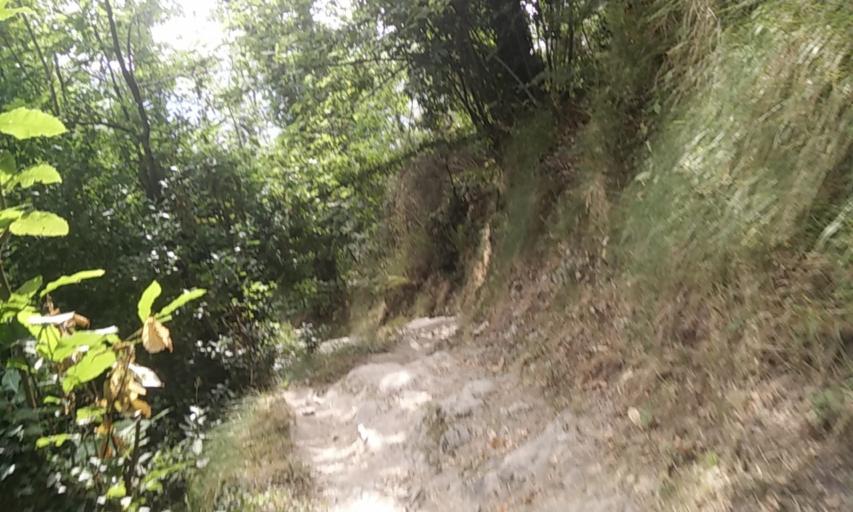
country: IT
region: Tuscany
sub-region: Provincia di Lucca
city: Pontestazzemese
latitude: 43.9955
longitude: 10.3234
